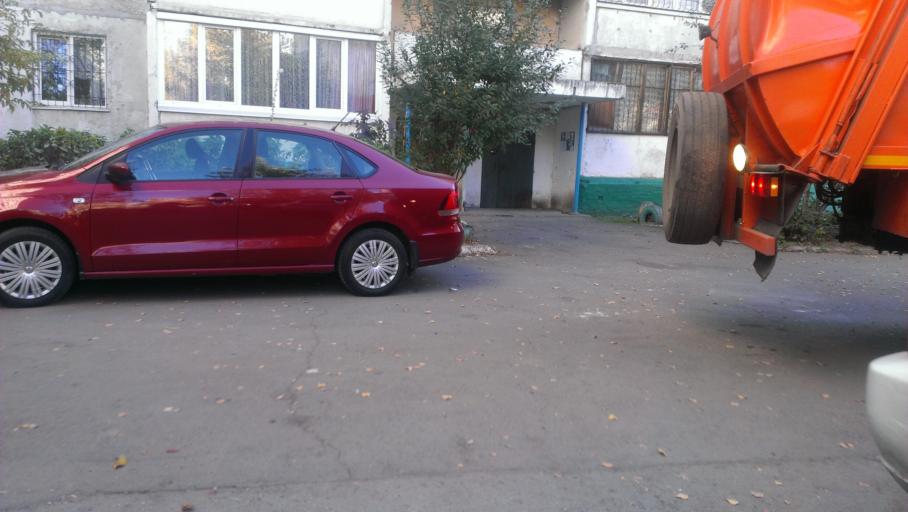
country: RU
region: Altai Krai
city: Novosilikatnyy
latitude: 53.3667
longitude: 83.6676
